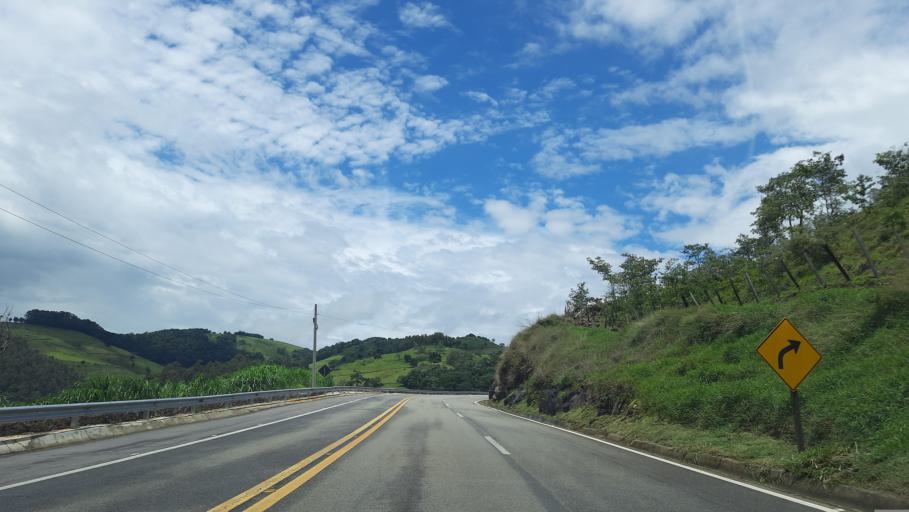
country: BR
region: Sao Paulo
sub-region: Vargem Grande Do Sul
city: Vargem Grande do Sul
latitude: -21.8323
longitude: -46.7566
